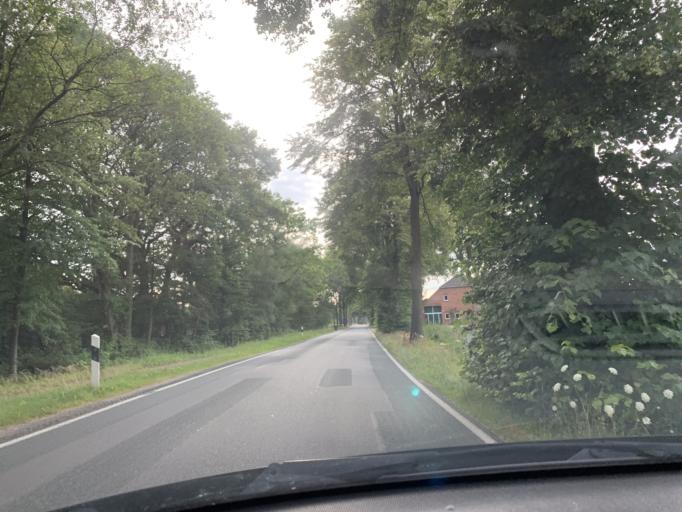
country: DE
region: Lower Saxony
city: Westerstede
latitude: 53.2754
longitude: 7.9339
